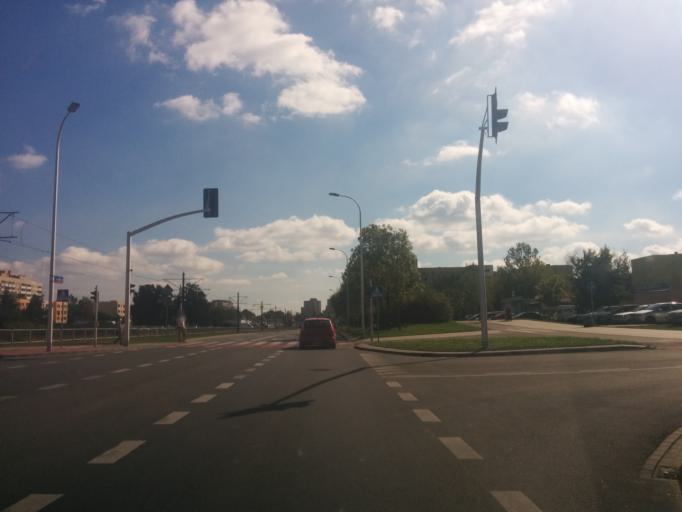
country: PL
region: Masovian Voivodeship
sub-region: Warszawa
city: Bialoleka
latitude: 52.3209
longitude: 20.9474
